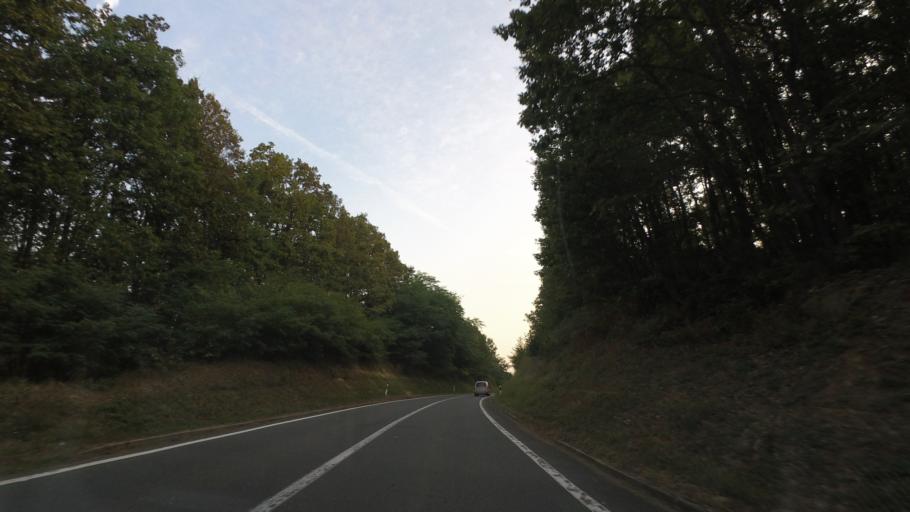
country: HR
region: Brodsko-Posavska
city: Cernik
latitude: 45.2772
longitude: 17.4023
